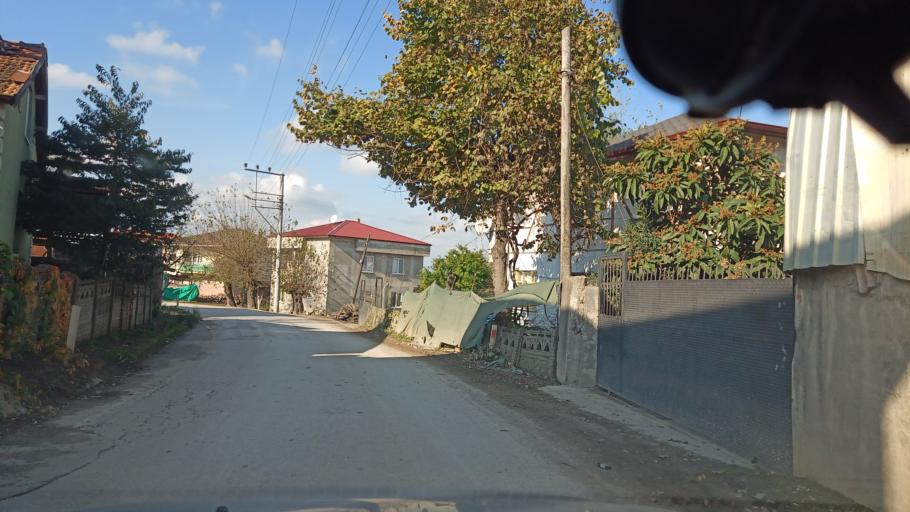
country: TR
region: Sakarya
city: Kaynarca
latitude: 41.0918
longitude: 30.4441
